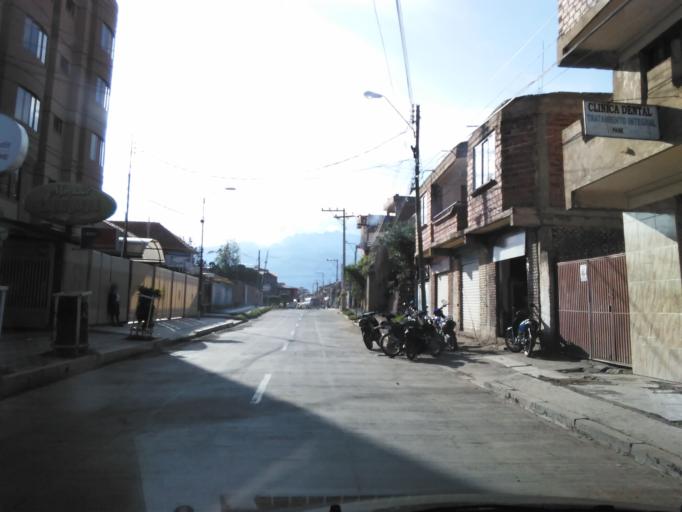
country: BO
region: Cochabamba
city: Cochabamba
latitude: -17.3382
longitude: -66.2176
